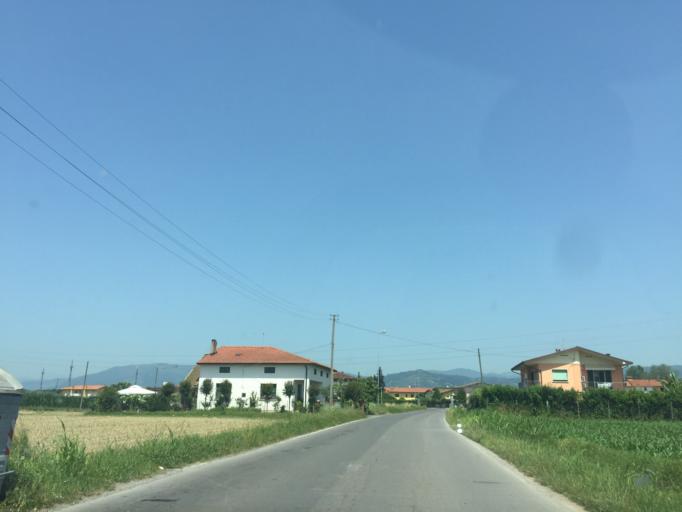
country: IT
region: Tuscany
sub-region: Provincia di Pistoia
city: Anchione
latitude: 43.8342
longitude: 10.7527
